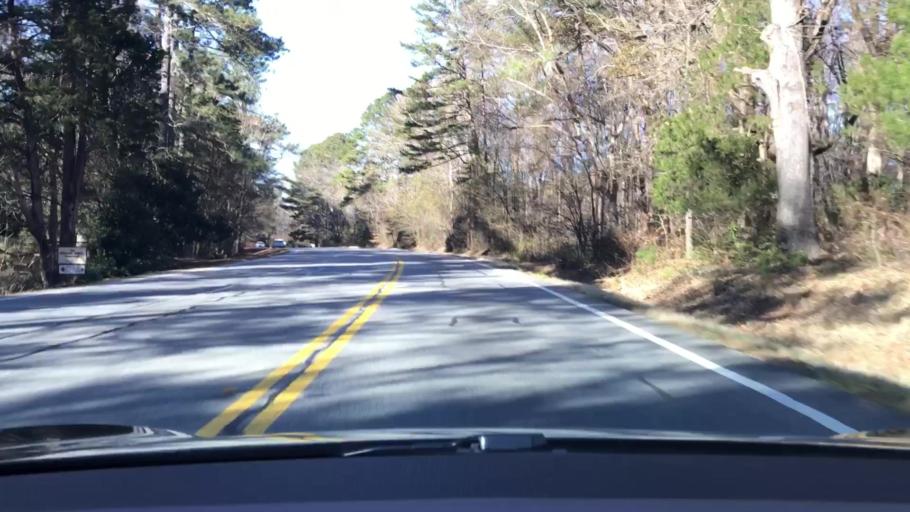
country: US
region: Georgia
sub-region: Barrow County
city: Russell
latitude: 33.8951
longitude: -83.7210
